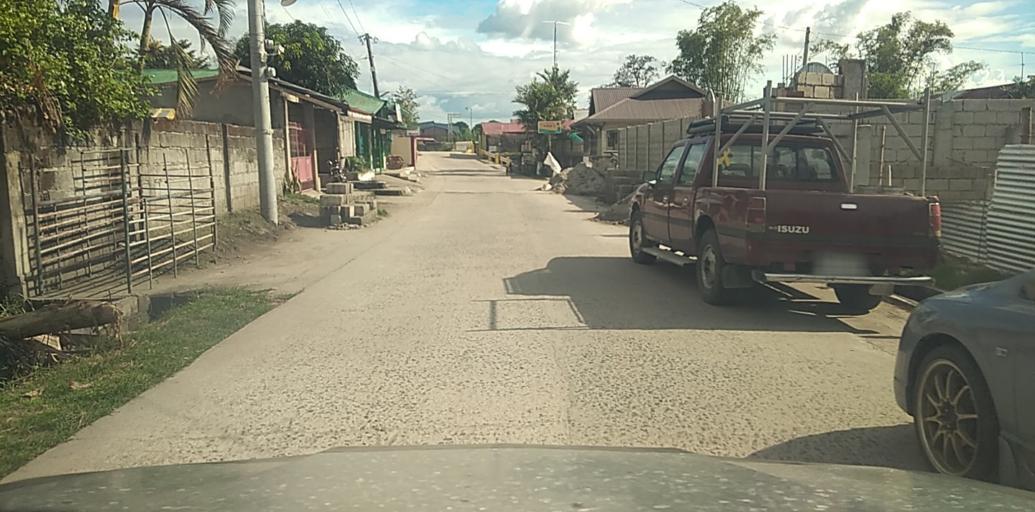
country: PH
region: Central Luzon
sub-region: Province of Pampanga
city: Panlinlang
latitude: 15.1869
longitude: 120.6932
